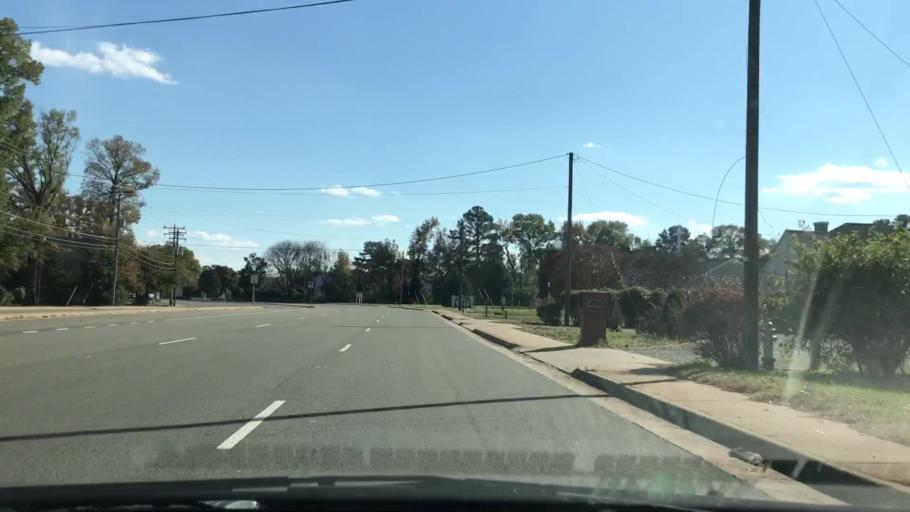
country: US
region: Virginia
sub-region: Henrico County
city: Dumbarton
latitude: 37.6063
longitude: -77.4948
